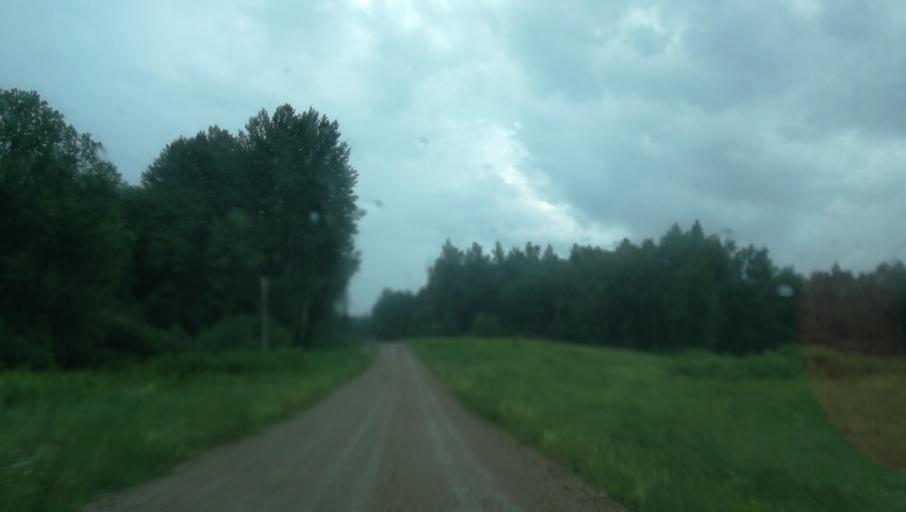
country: LV
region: Vecpiebalga
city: Vecpiebalga
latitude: 57.1058
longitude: 25.6915
